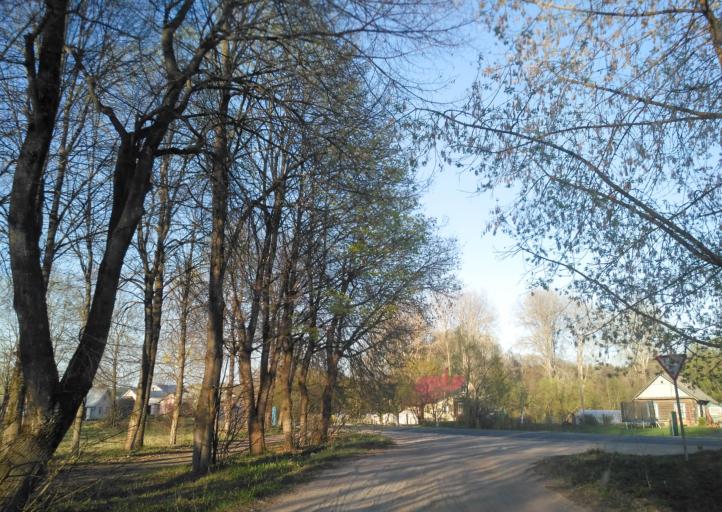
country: BY
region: Minsk
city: Pyatryshki
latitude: 54.1098
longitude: 27.1878
